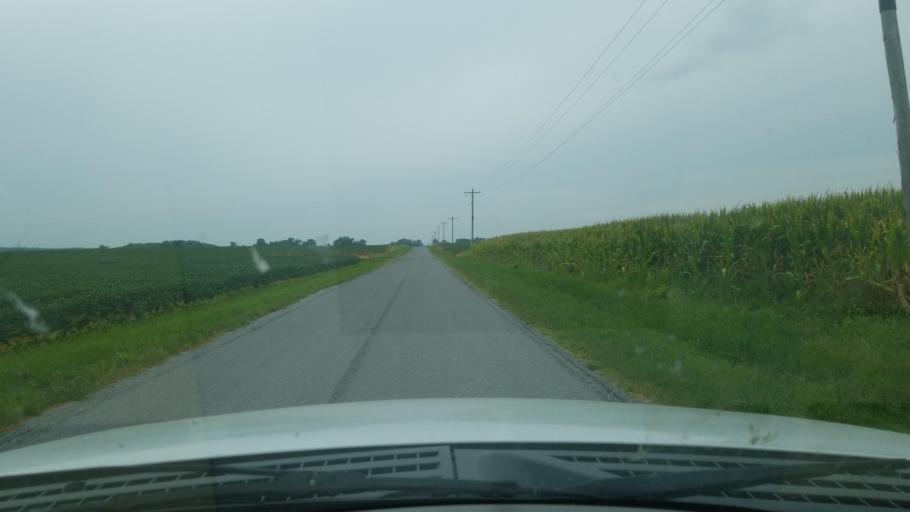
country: US
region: Illinois
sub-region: Saline County
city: Eldorado
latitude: 37.8669
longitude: -88.4746
